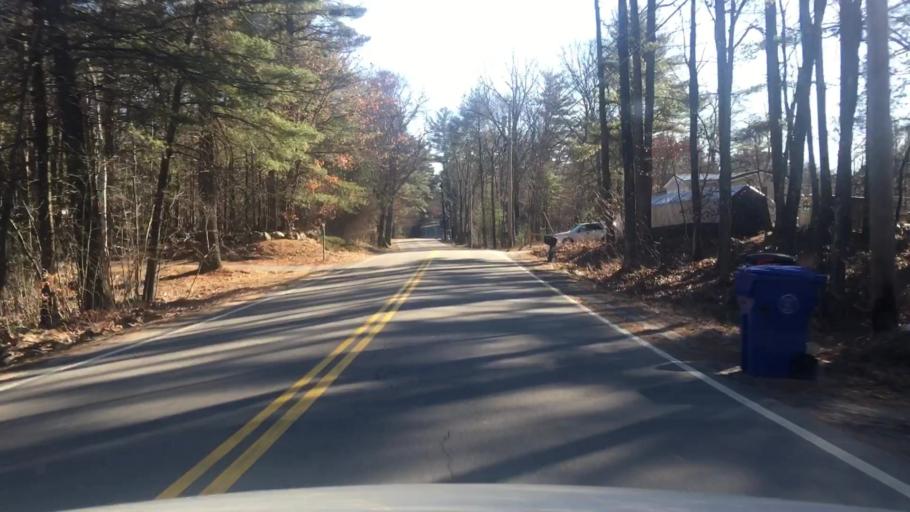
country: US
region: New Hampshire
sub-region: Rockingham County
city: Londonderry
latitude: 42.8923
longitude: -71.4108
